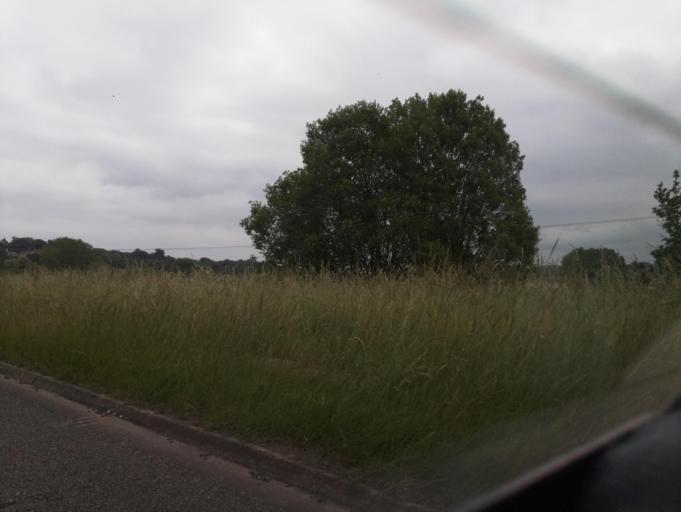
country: GB
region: England
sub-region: District of Rutland
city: Burley
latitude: 52.6743
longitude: -0.6758
